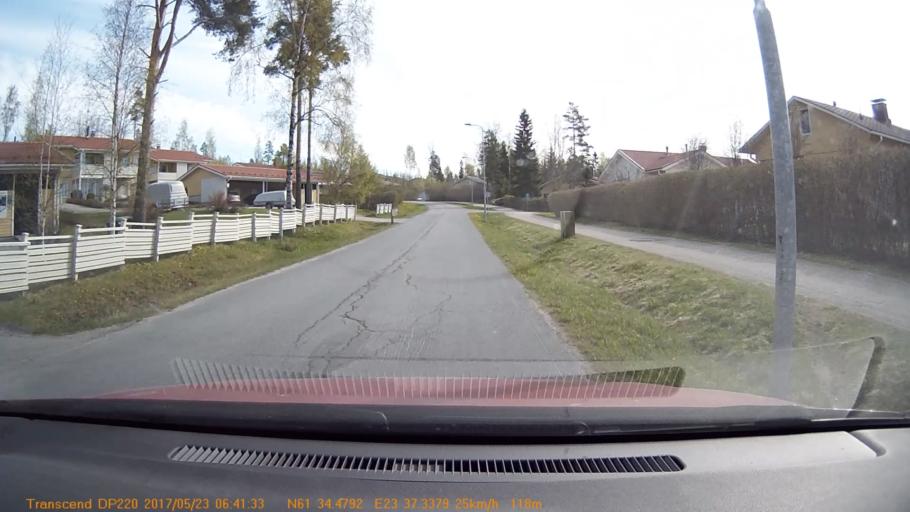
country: FI
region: Pirkanmaa
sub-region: Tampere
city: Yloejaervi
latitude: 61.5746
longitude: 23.6220
